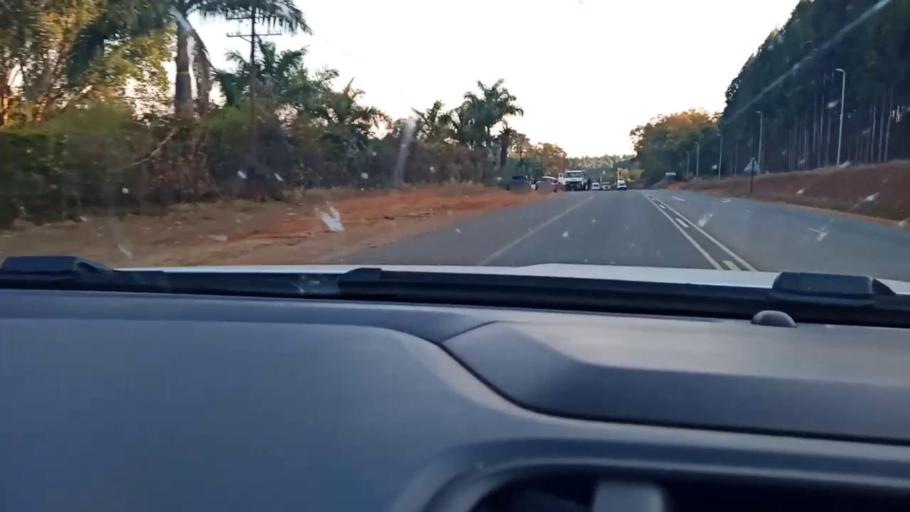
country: ZA
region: Limpopo
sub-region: Mopani District Municipality
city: Duiwelskloof
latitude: -23.7024
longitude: 30.1346
